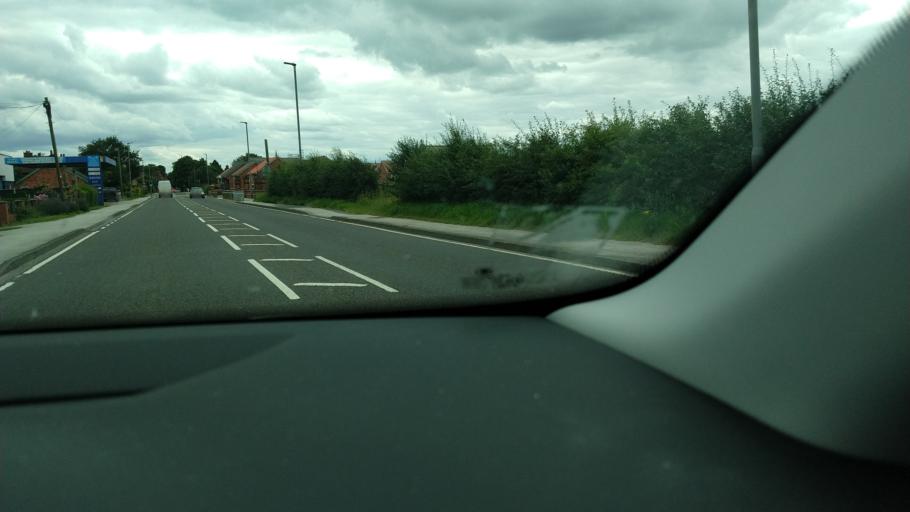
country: GB
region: England
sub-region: North Yorkshire
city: Camblesforth
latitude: 53.7138
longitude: -1.0194
